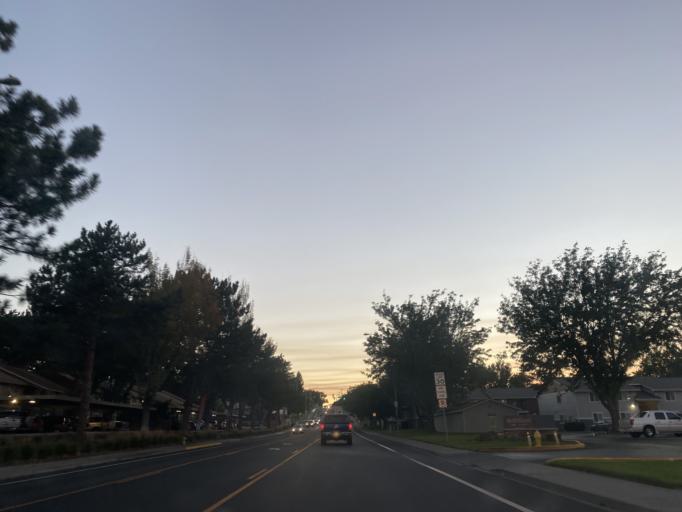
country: US
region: Washington
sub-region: Benton County
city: Kennewick
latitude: 46.1986
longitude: -119.1338
